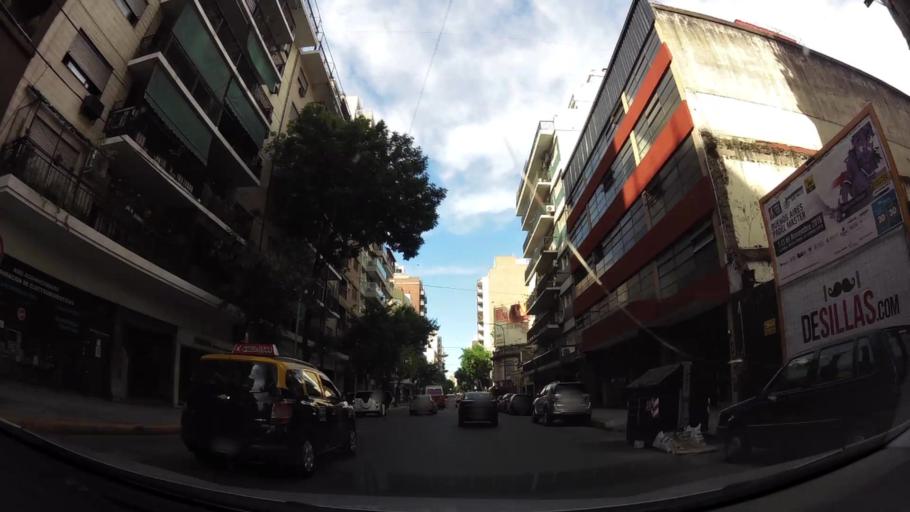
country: AR
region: Buenos Aires F.D.
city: Colegiales
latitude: -34.5592
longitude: -58.4613
